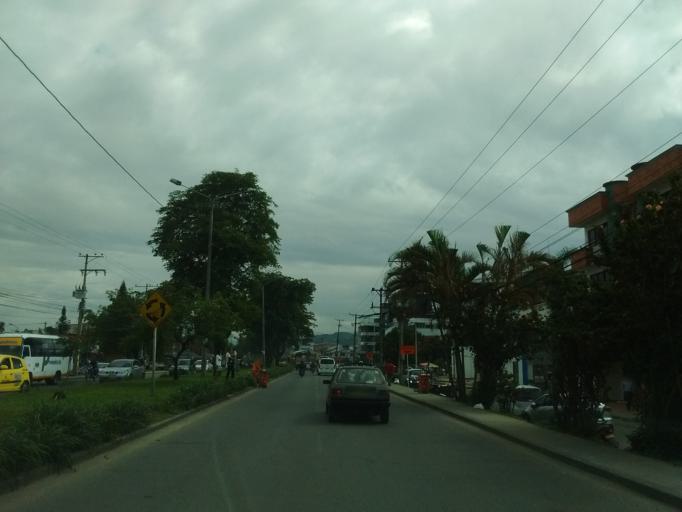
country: CO
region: Cauca
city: Popayan
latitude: 2.4547
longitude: -76.5988
